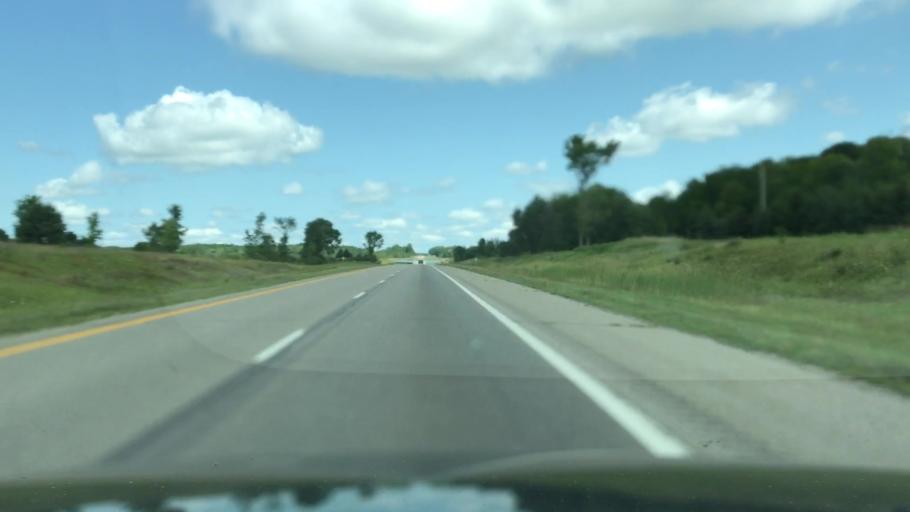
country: US
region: Michigan
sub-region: Mecosta County
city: Big Rapids
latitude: 43.7087
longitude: -85.5289
